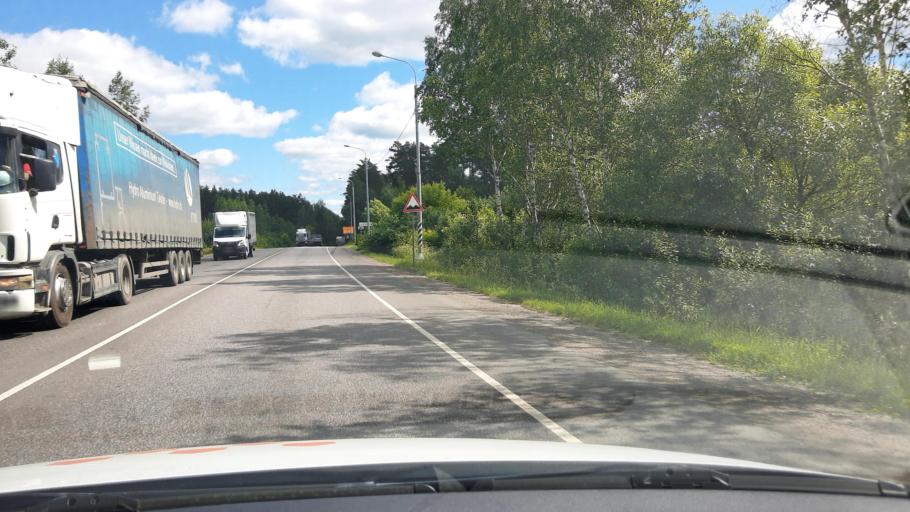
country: RU
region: Moskovskaya
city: Noginsk
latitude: 55.8664
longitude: 38.4184
